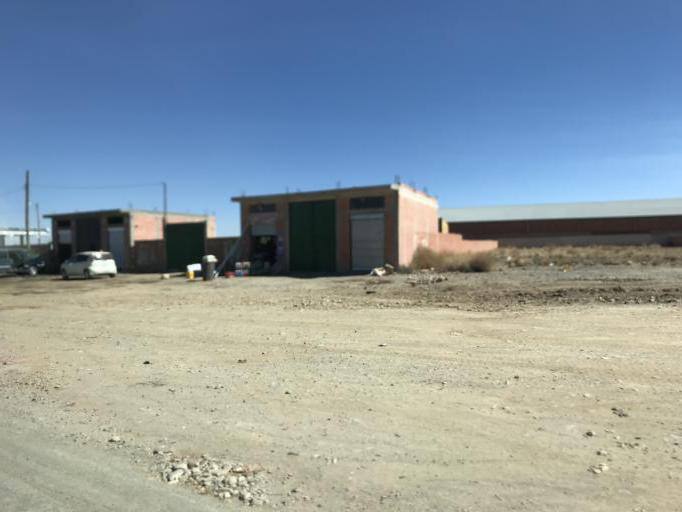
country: BO
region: La Paz
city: La Paz
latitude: -16.5108
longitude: -68.2707
